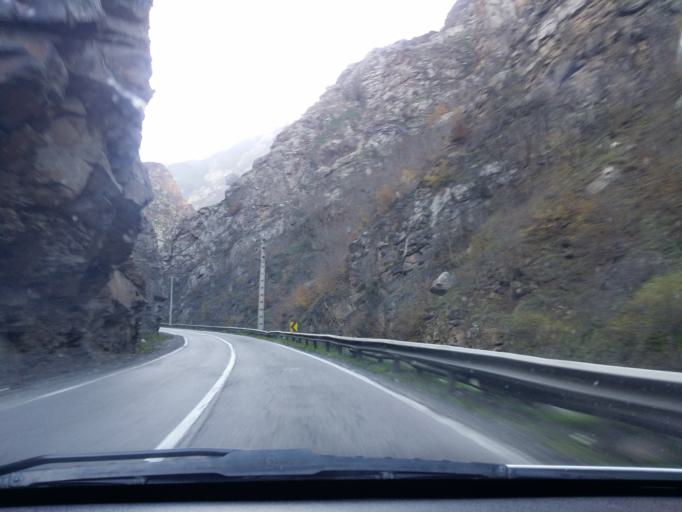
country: IR
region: Mazandaran
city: Chalus
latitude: 36.2837
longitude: 51.2421
